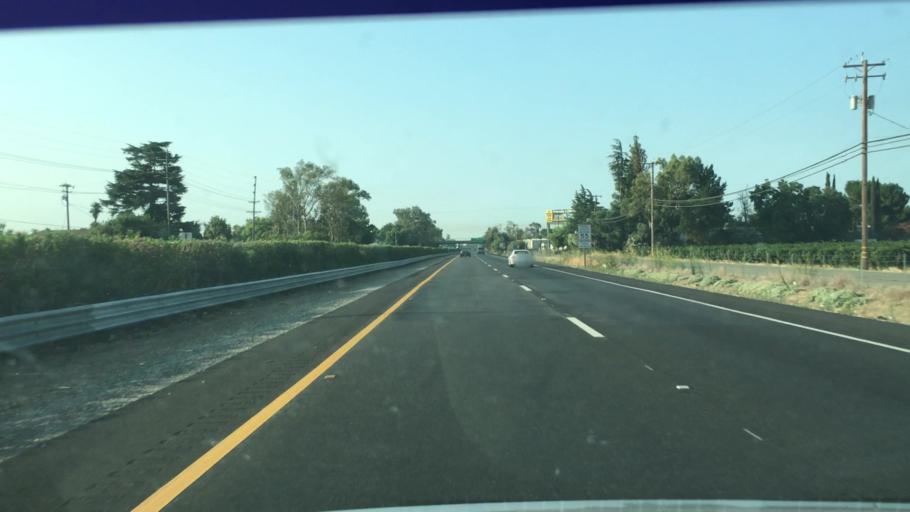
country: US
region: California
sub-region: San Joaquin County
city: Lodi
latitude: 38.1652
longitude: -121.2621
